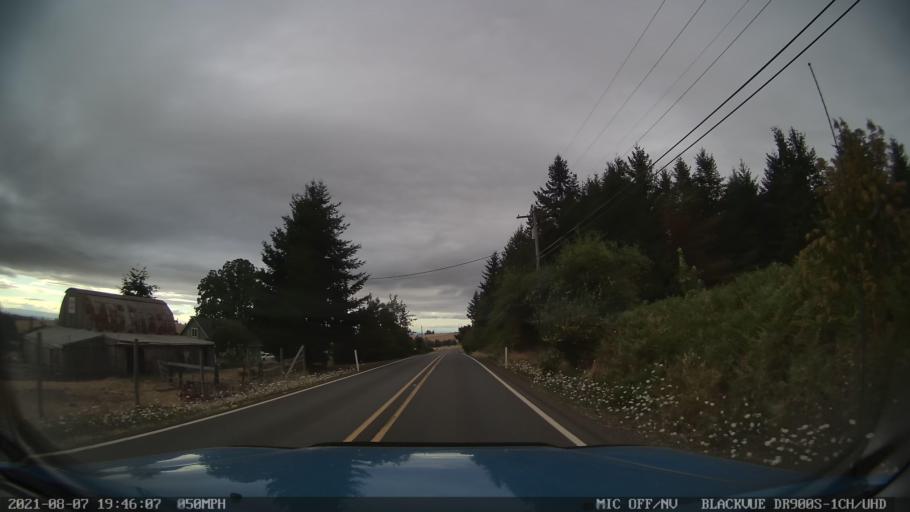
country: US
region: Oregon
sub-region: Marion County
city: Silverton
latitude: 44.9552
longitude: -122.7011
